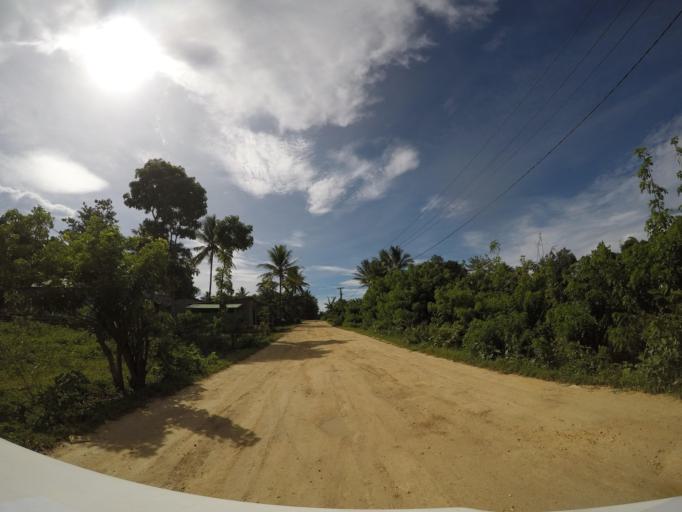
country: TL
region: Lautem
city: Lospalos
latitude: -8.4987
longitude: 126.9975
